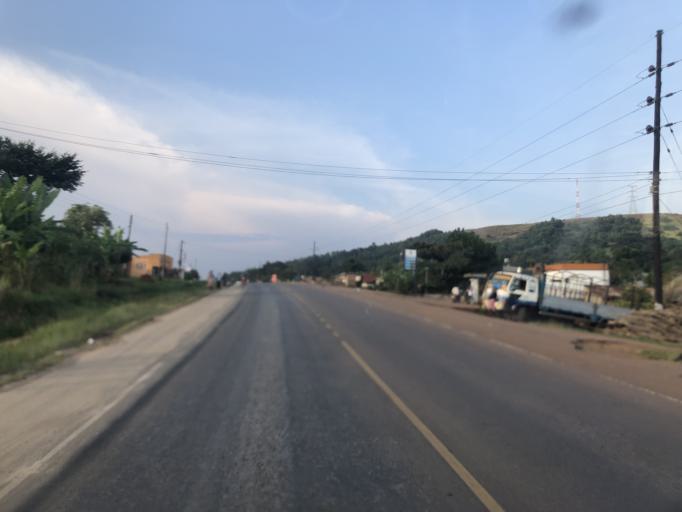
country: UG
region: Central Region
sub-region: Mpigi District
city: Mpigi
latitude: 0.1906
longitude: 32.2940
